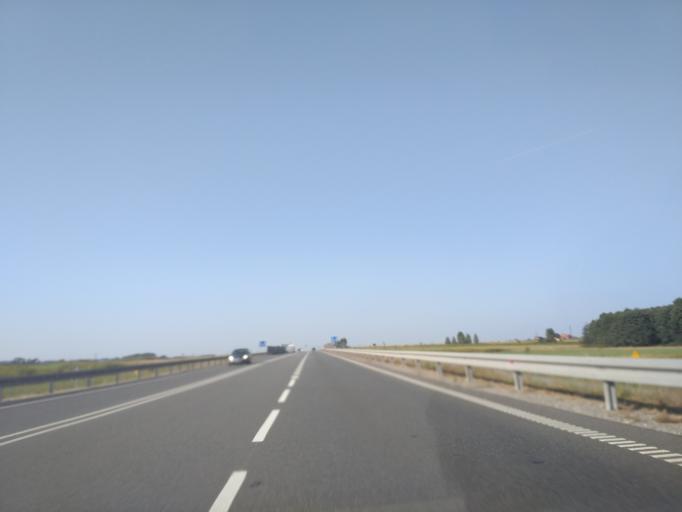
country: PL
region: Subcarpathian Voivodeship
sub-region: Powiat rzeszowski
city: Sokolow Malopolski
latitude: 50.2164
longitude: 22.1267
